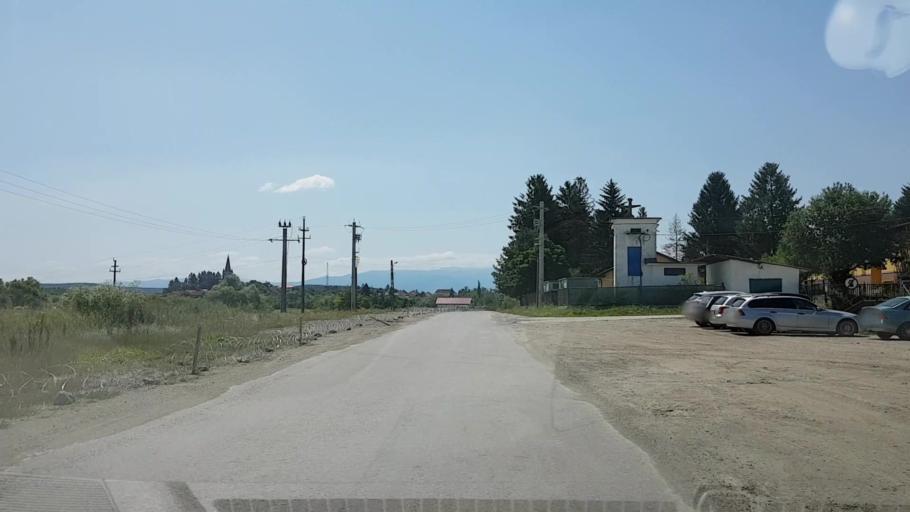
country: RO
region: Brasov
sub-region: Comuna Cincu
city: Cincu
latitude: 45.9252
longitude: 24.7969
